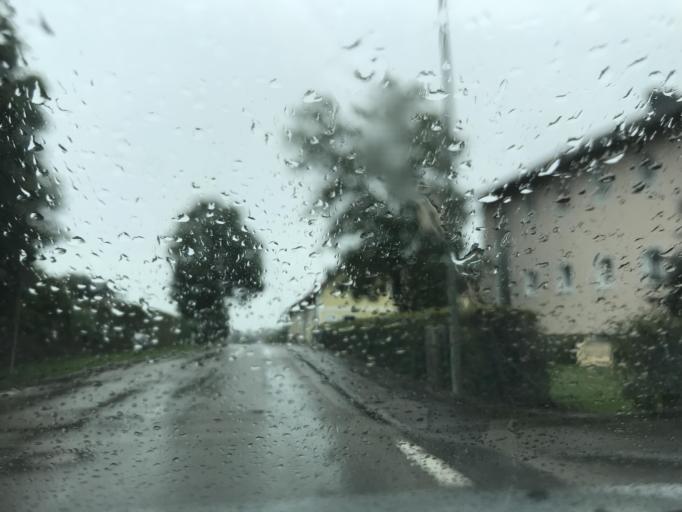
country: DE
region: Bavaria
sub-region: Upper Bavaria
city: Jetzendorf
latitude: 48.4339
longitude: 11.4383
